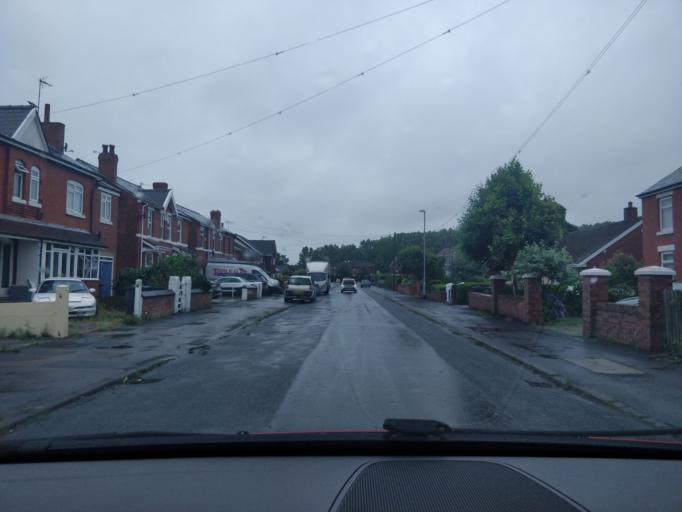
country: GB
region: England
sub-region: Lancashire
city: Banks
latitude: 53.6778
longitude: -2.9260
